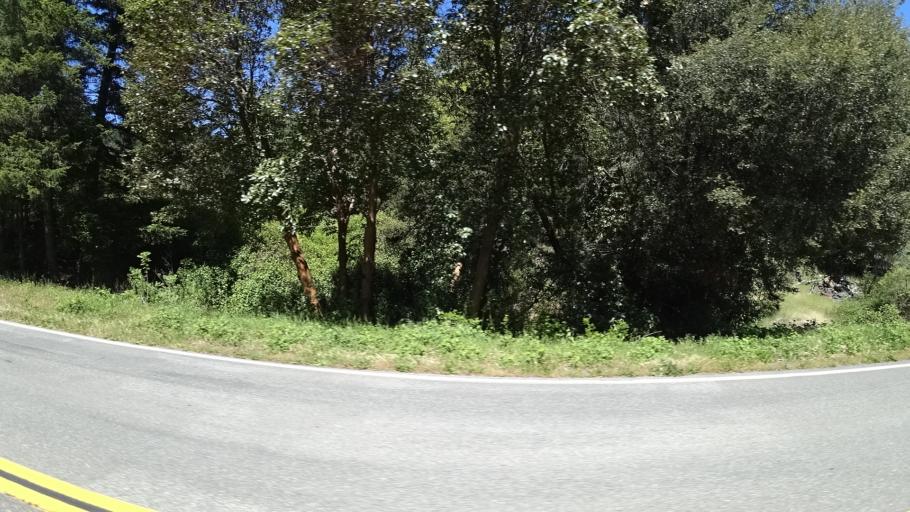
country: US
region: California
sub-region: Trinity County
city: Hayfork
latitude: 40.7395
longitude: -123.2509
